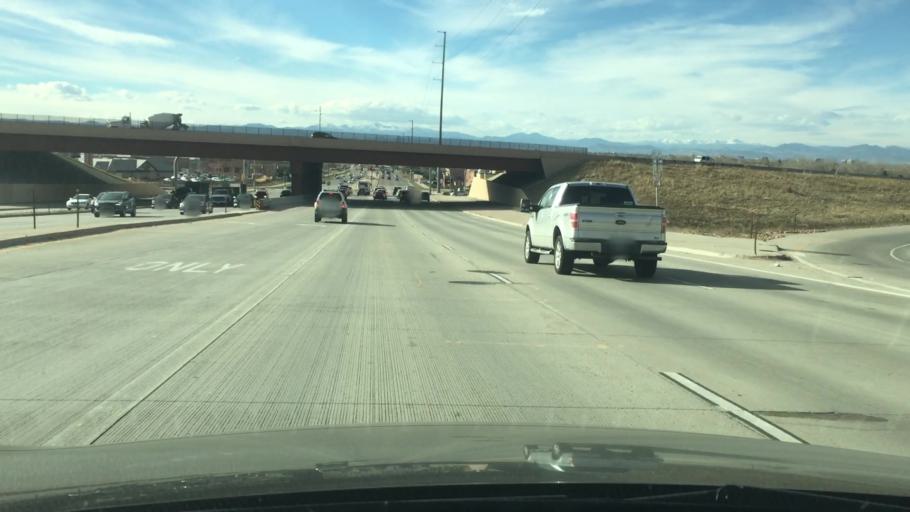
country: US
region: Colorado
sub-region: Arapahoe County
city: Dove Valley
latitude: 39.5951
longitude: -104.8007
